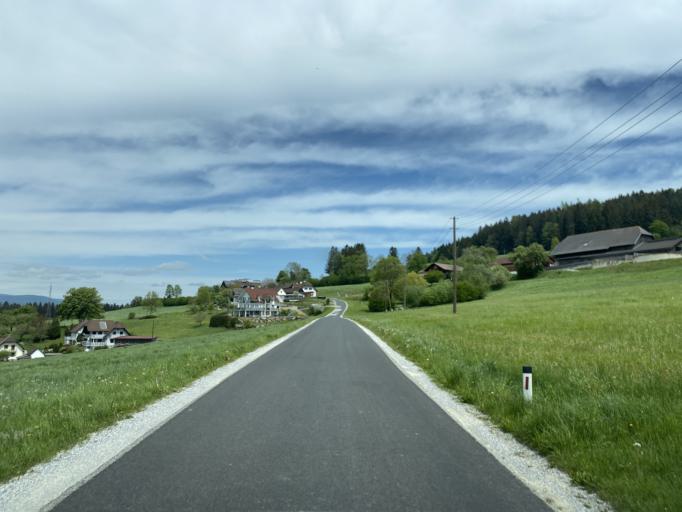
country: AT
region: Styria
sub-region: Politischer Bezirk Weiz
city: Gschaid bei Birkfeld
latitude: 47.3523
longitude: 15.7211
